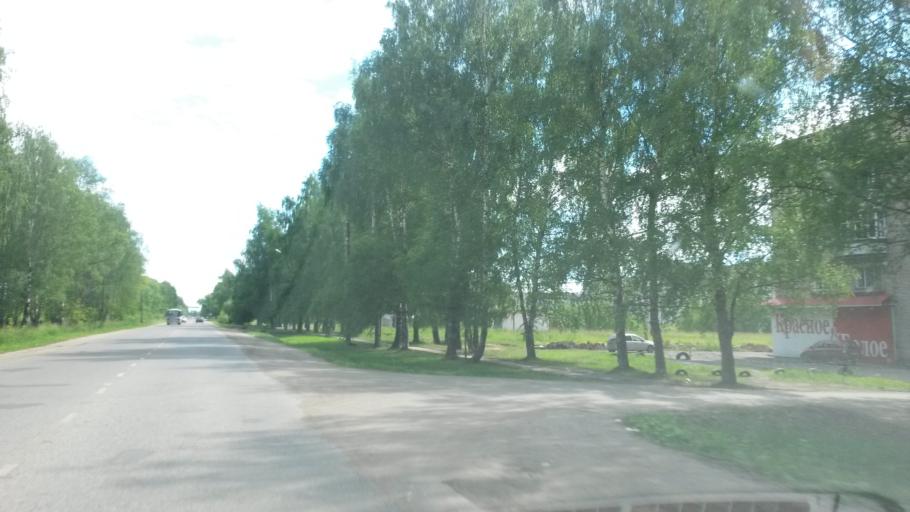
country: RU
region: Ivanovo
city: Zavolzhsk
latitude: 57.4777
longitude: 42.1518
